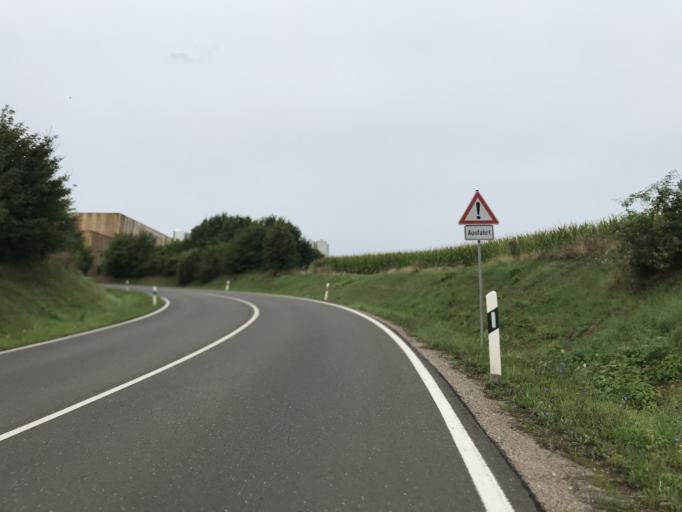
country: DE
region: Rheinland-Pfalz
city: Zotzenheim
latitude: 49.8650
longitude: 7.9730
